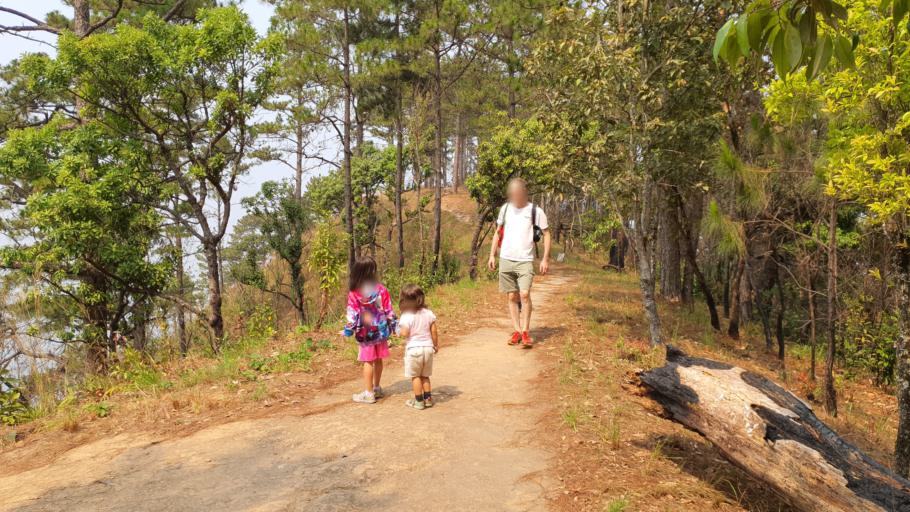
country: TH
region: Chiang Mai
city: Chiang Mai
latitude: 18.8358
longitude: 98.8888
